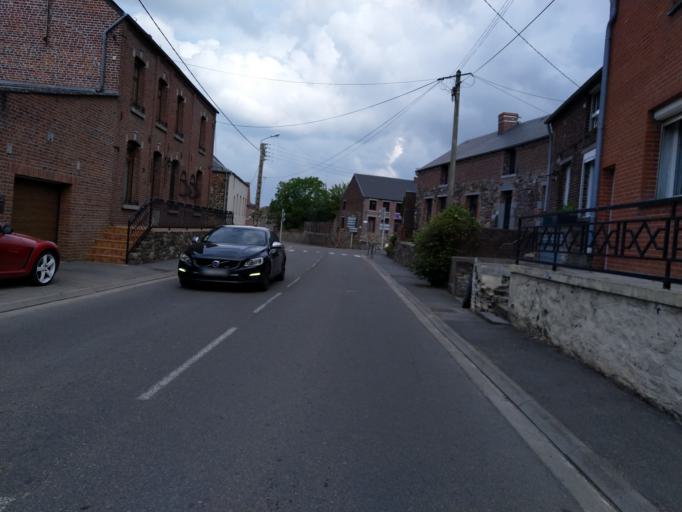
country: FR
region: Nord-Pas-de-Calais
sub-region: Departement du Nord
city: Boussois
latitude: 50.3375
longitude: 4.0145
